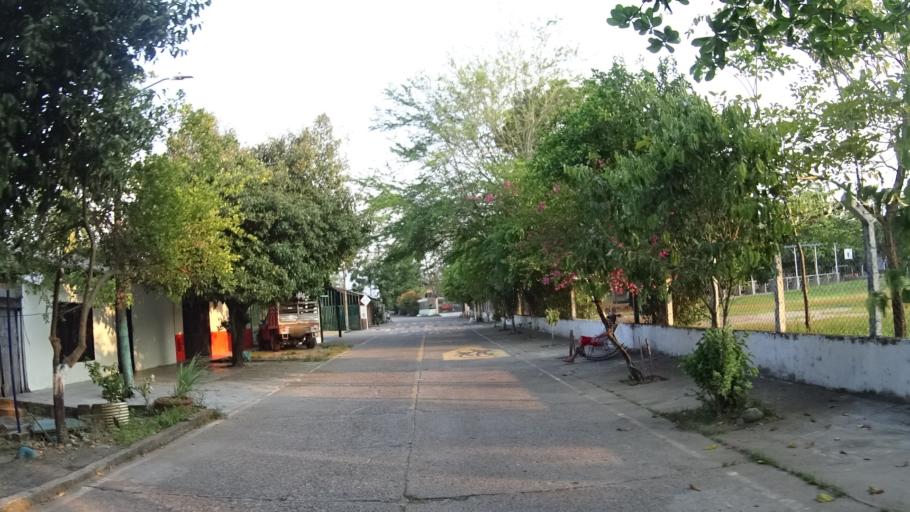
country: CO
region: Cundinamarca
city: Puerto Salgar
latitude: 5.4784
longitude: -74.6686
